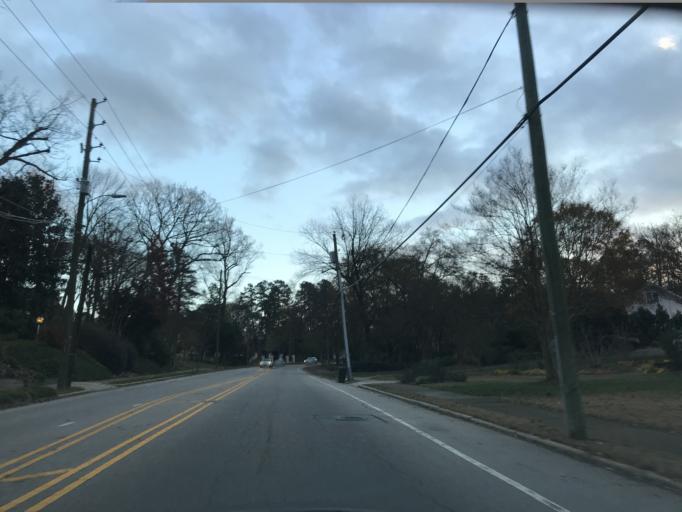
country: US
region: North Carolina
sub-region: Wake County
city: West Raleigh
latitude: 35.8220
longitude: -78.6509
